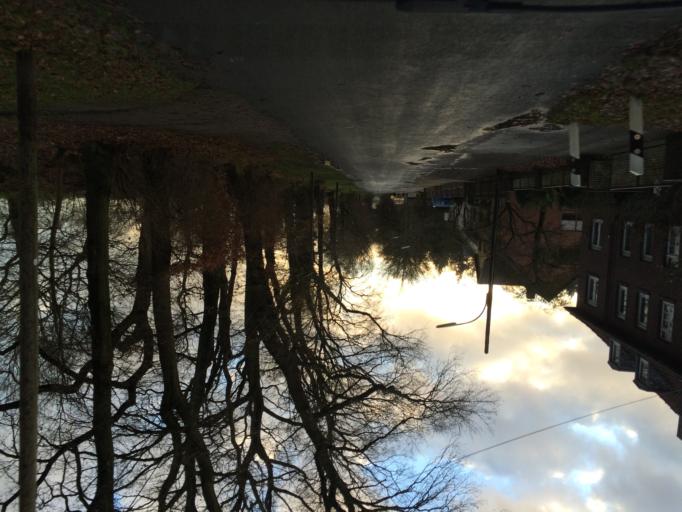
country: DE
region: North Rhine-Westphalia
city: Dorsten
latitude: 51.6852
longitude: 7.0139
